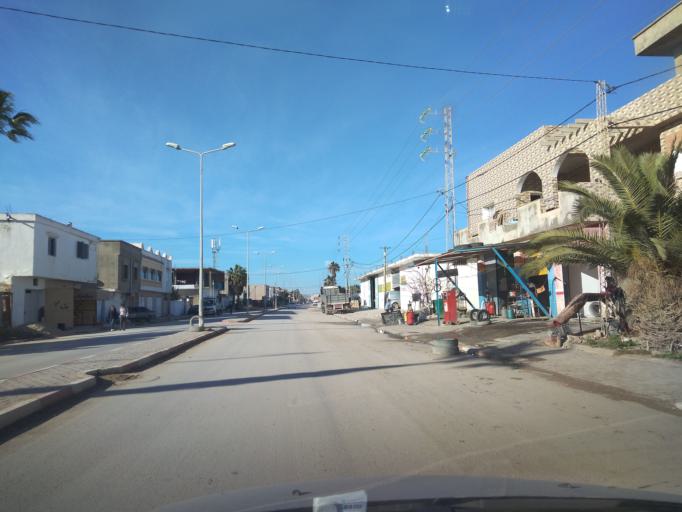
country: TN
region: Ariana
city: Qal'at al Andalus
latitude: 37.0550
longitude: 10.1212
